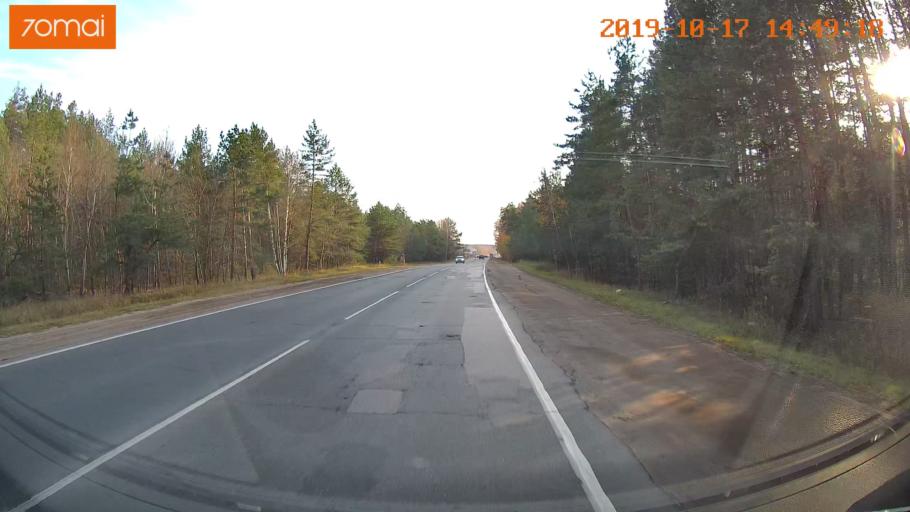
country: RU
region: Rjazan
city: Polyany
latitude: 54.7487
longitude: 39.8396
